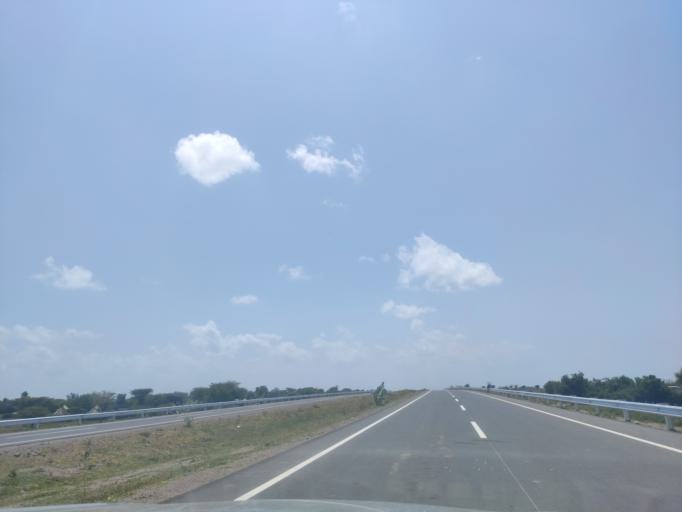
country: ET
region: Oromiya
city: Mojo
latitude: 8.3495
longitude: 38.9830
